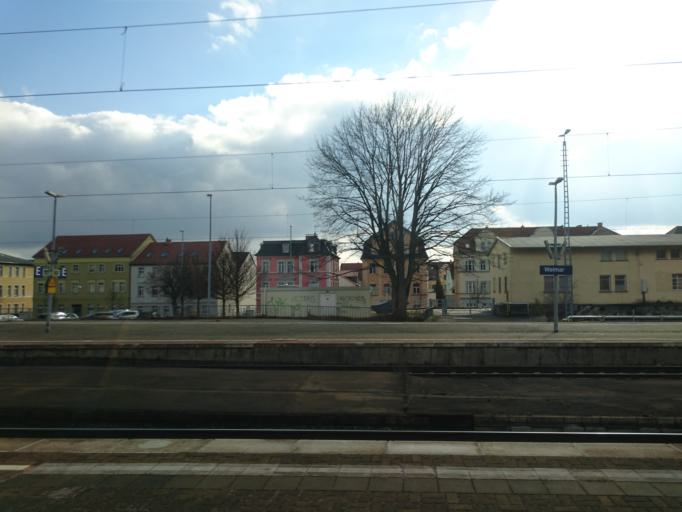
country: DE
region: Thuringia
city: Weimar
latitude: 50.9917
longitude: 11.3241
